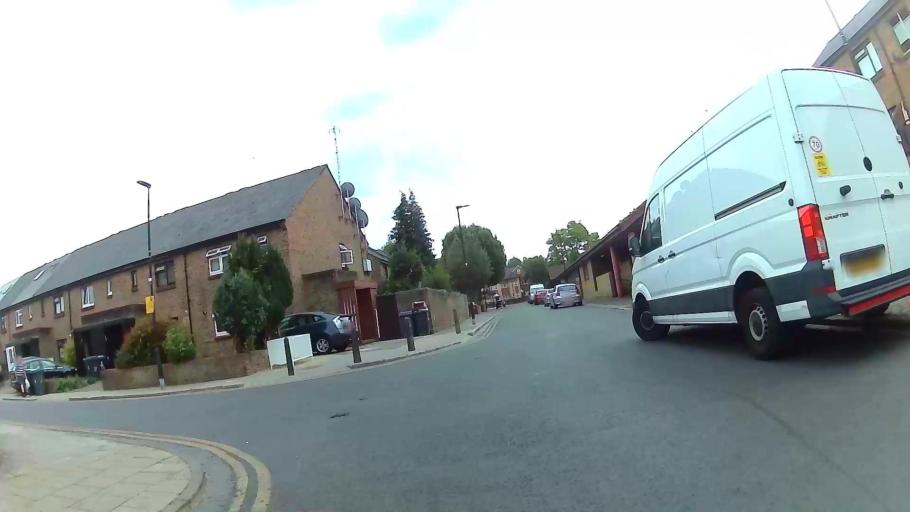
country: GB
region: England
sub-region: Greater London
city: Harringay
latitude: 51.5783
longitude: -0.0744
